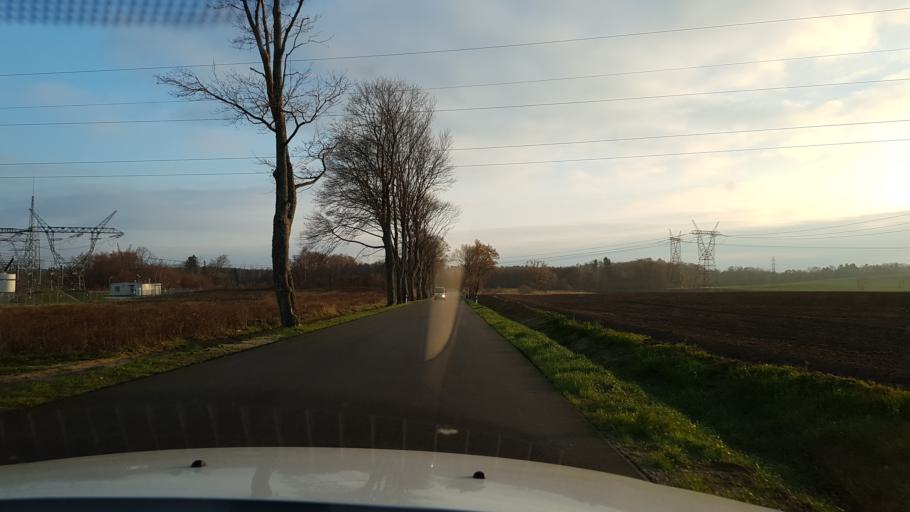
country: PL
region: West Pomeranian Voivodeship
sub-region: Koszalin
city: Koszalin
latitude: 54.1286
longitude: 16.0884
